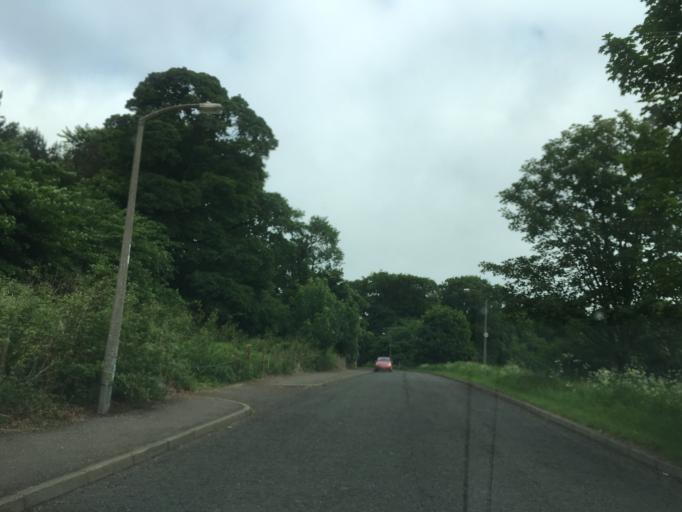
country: GB
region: Scotland
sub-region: Midlothian
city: Loanhead
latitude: 55.9026
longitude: -3.1905
